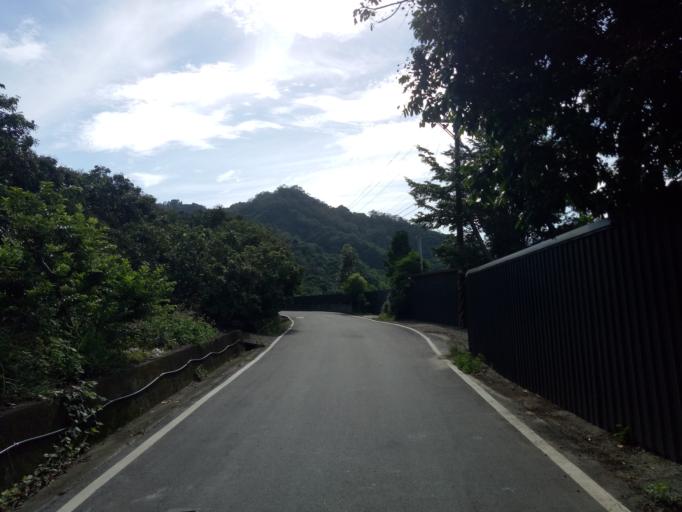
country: TW
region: Taiwan
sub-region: Taichung City
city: Taichung
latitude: 24.0854
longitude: 120.7460
